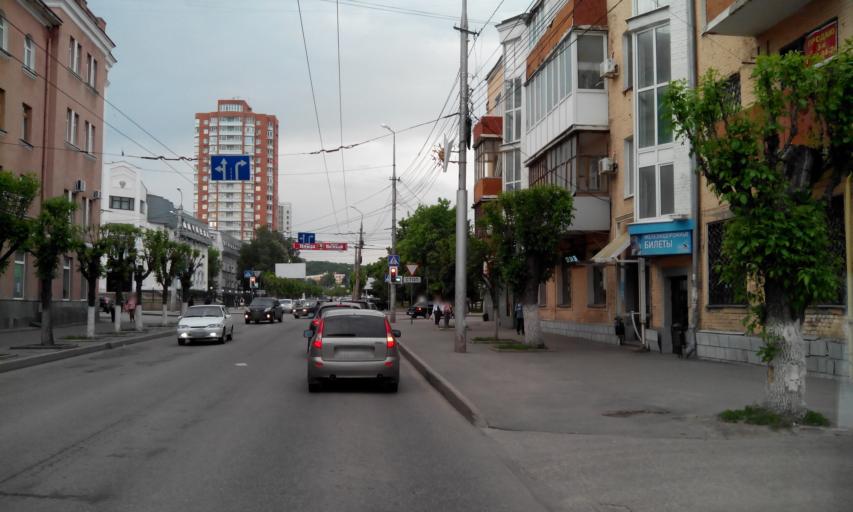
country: RU
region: Penza
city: Penza
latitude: 53.1924
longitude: 45.0147
